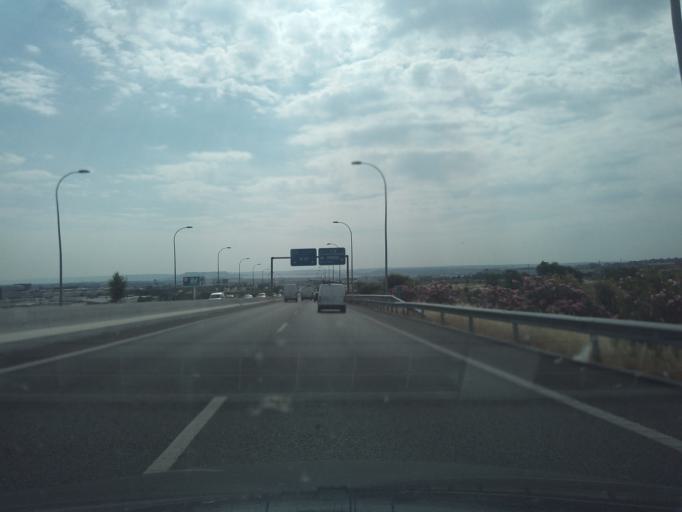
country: ES
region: Madrid
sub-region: Provincia de Madrid
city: Coslada
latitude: 40.4403
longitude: -3.5724
